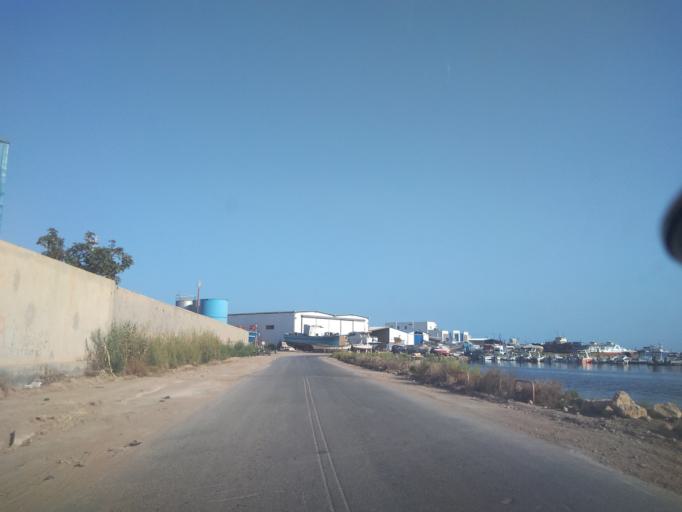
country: TN
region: Safaqis
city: Sfax
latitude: 34.7207
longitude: 10.7668
